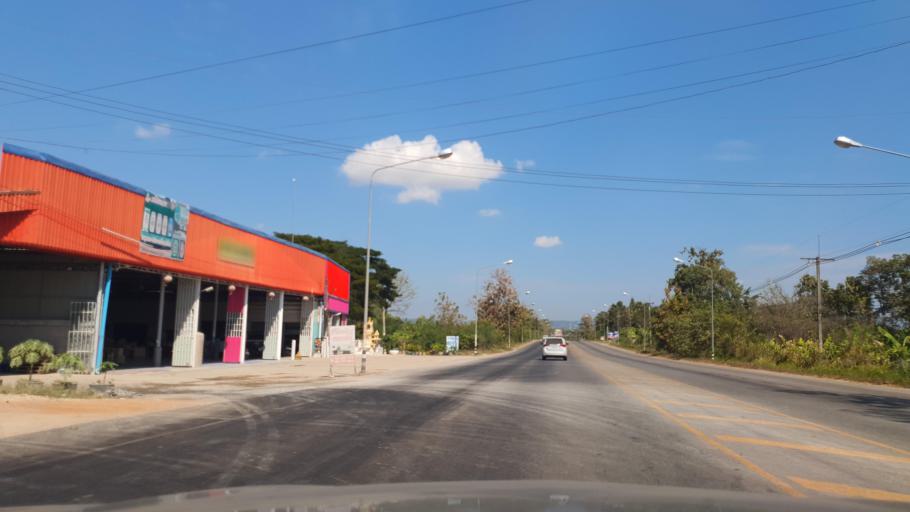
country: TH
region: Kalasin
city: Somdet
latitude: 16.7334
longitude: 103.7654
